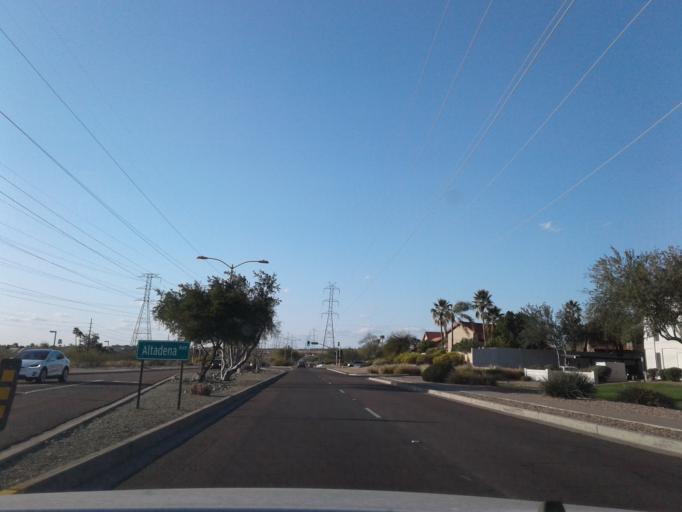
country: US
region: Arizona
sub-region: Maricopa County
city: Scottsdale
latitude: 33.5907
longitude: -111.8375
